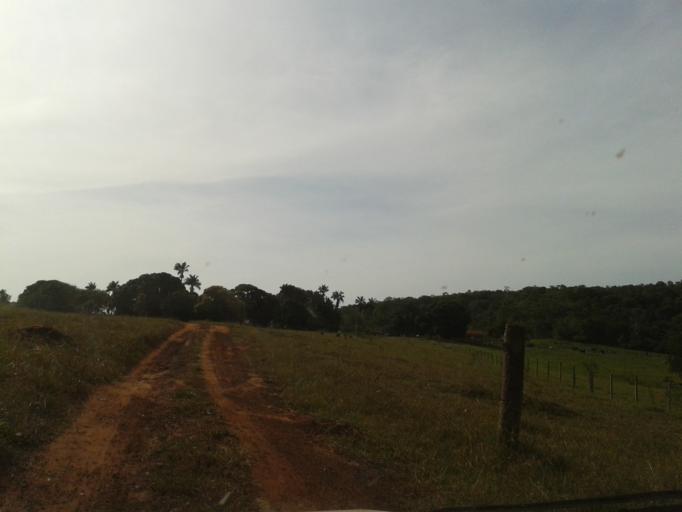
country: BR
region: Minas Gerais
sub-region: Campina Verde
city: Campina Verde
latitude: -19.4953
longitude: -49.5758
